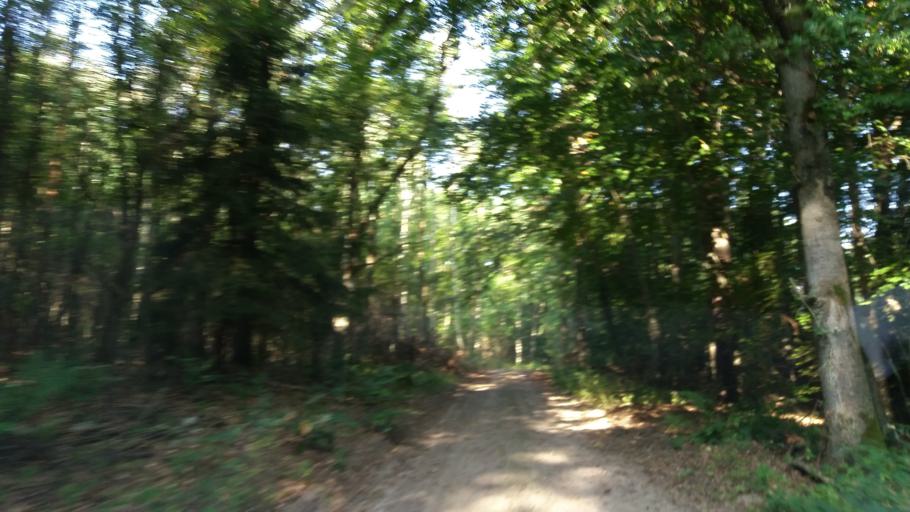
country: PL
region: West Pomeranian Voivodeship
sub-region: Powiat choszczenski
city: Choszczno
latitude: 53.2359
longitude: 15.4394
